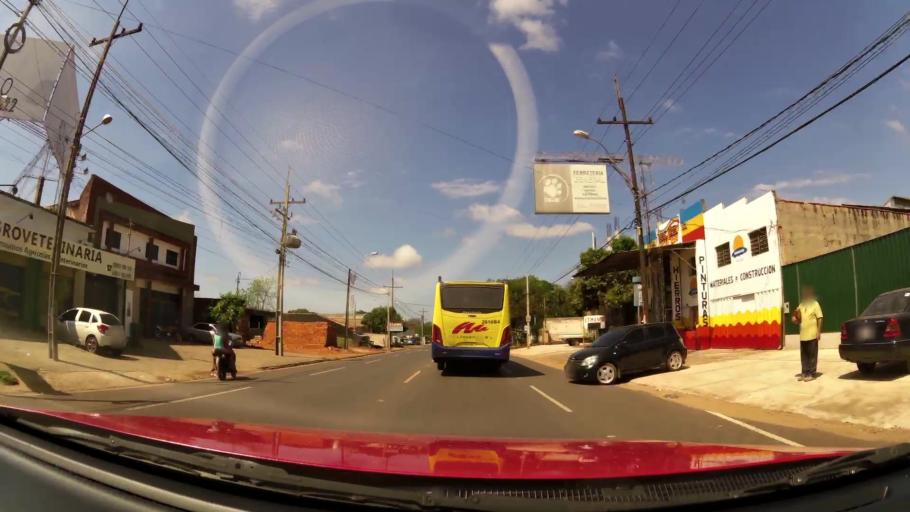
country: PY
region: Central
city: San Lorenzo
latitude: -25.2962
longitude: -57.5025
